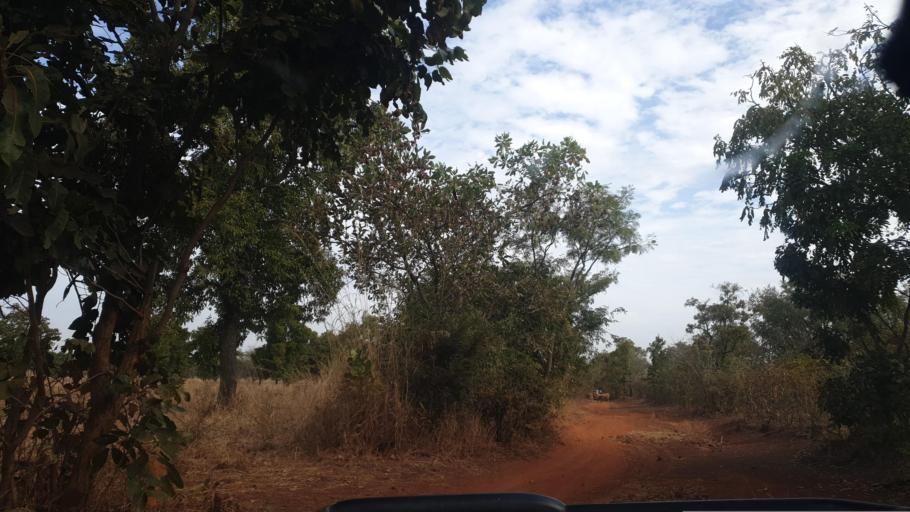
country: ML
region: Sikasso
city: Yanfolila
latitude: 11.4012
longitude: -8.0154
